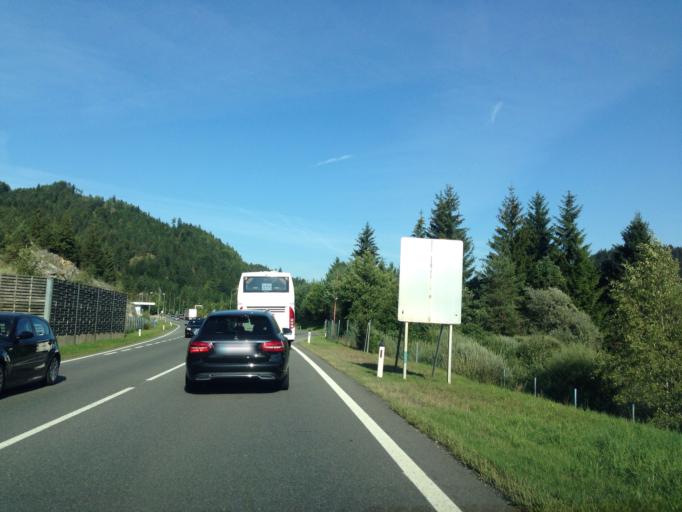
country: AT
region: Tyrol
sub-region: Politischer Bezirk Reutte
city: Musau
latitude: 47.5381
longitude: 10.6715
